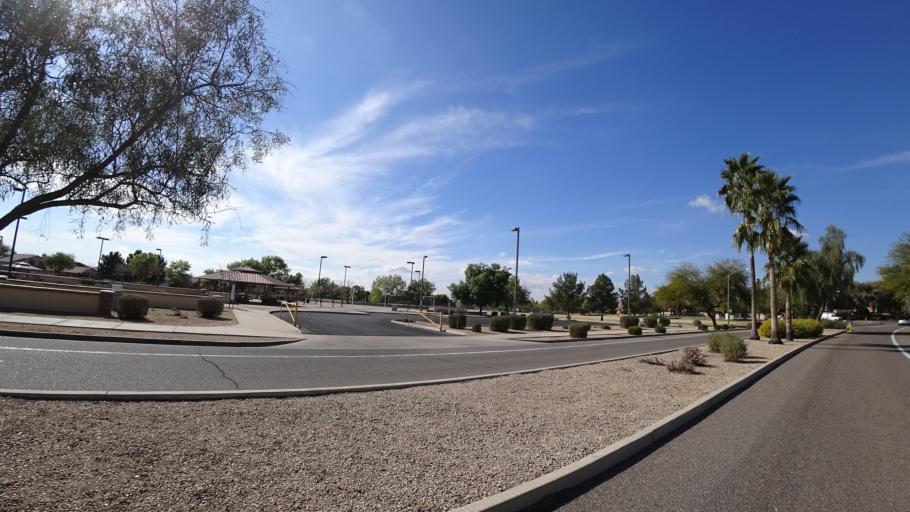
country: US
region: Arizona
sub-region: Maricopa County
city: Peoria
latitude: 33.6738
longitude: -112.2124
